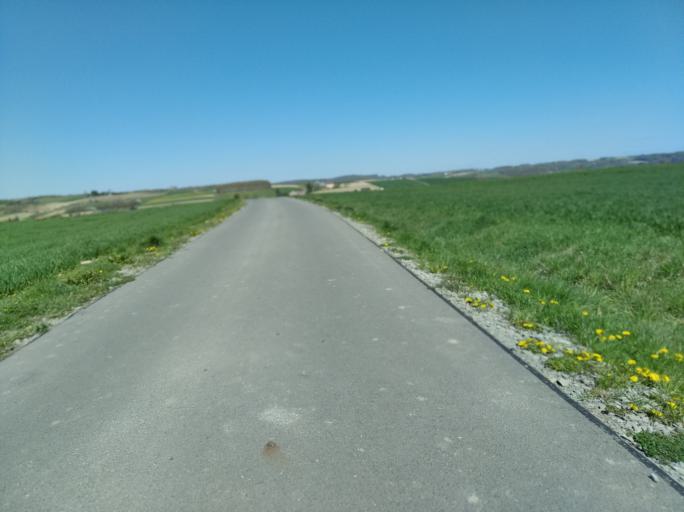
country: PL
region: Subcarpathian Voivodeship
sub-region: Powiat strzyzowski
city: Wisniowa
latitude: 49.9049
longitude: 21.6864
